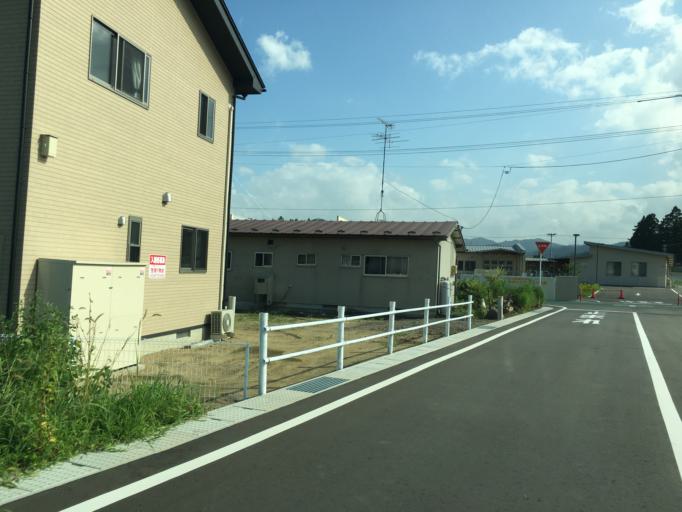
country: JP
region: Miyagi
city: Marumori
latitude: 37.9258
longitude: 140.7664
